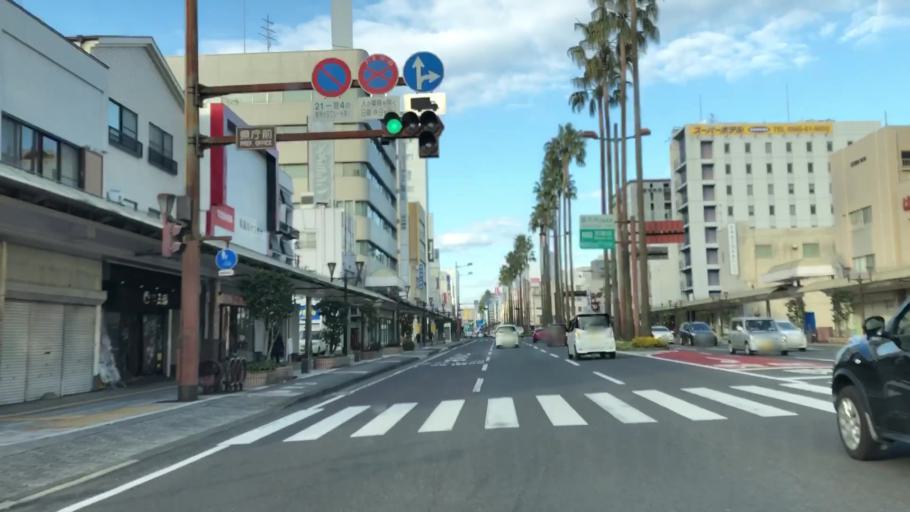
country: JP
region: Miyazaki
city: Miyazaki-shi
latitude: 31.9102
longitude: 131.4220
